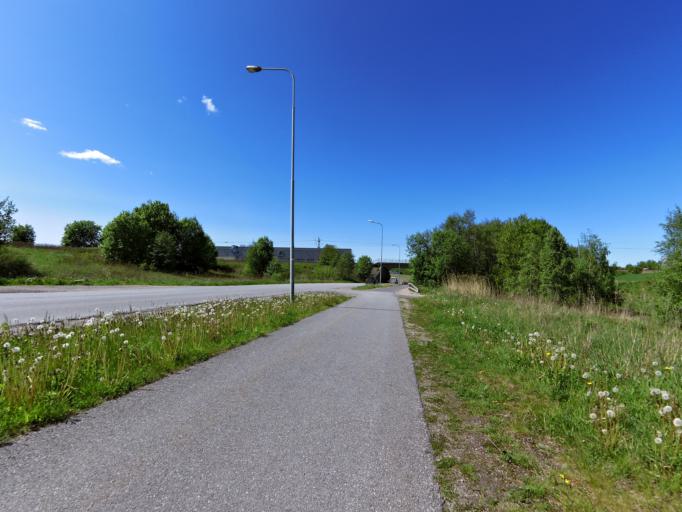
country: NO
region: Ostfold
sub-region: Fredrikstad
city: Fredrikstad
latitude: 59.2401
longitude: 10.9865
